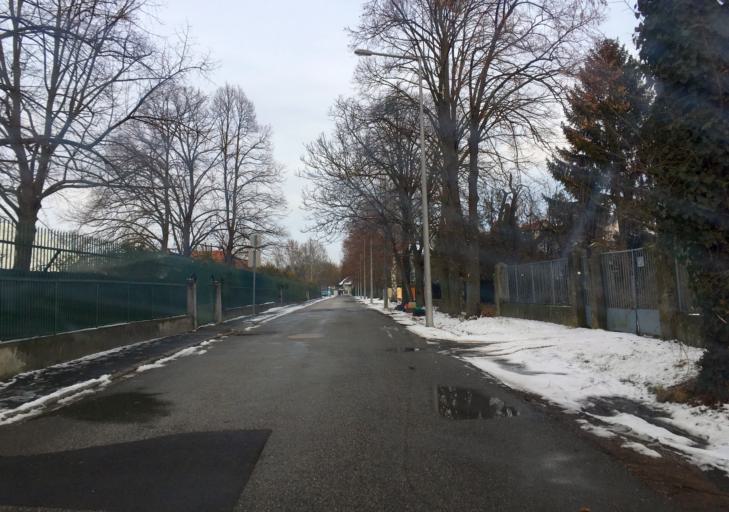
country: HU
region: Gyor-Moson-Sopron
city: Mosonmagyarovar
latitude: 47.8756
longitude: 17.2777
